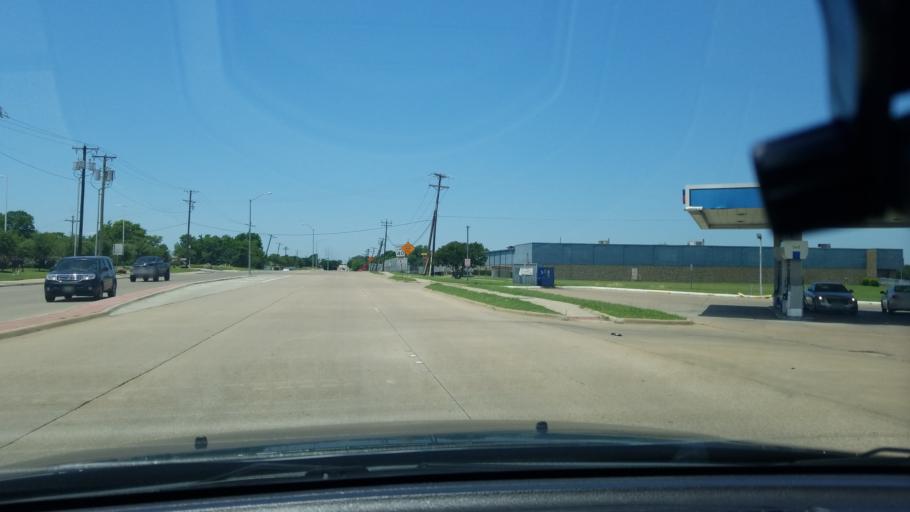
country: US
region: Texas
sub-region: Dallas County
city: Mesquite
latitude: 32.7924
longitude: -96.6563
